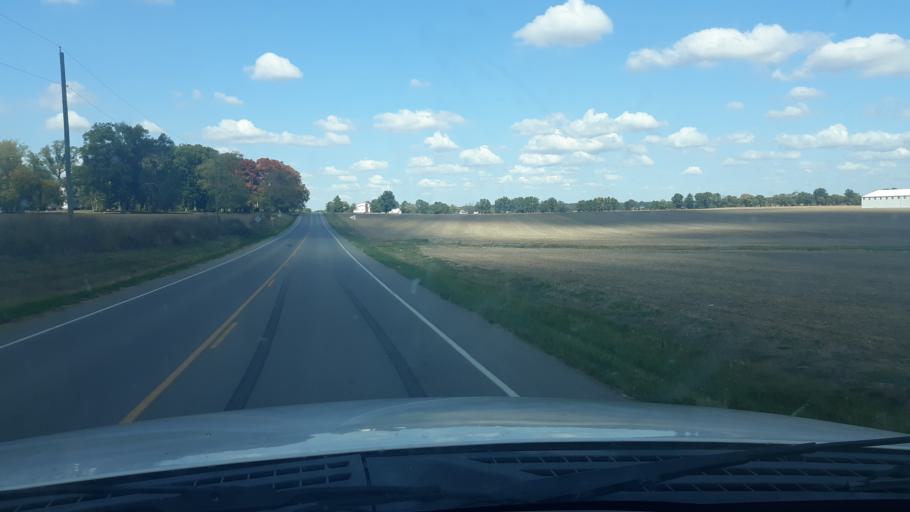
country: US
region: Illinois
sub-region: Saline County
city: Eldorado
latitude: 37.7903
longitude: -88.4848
